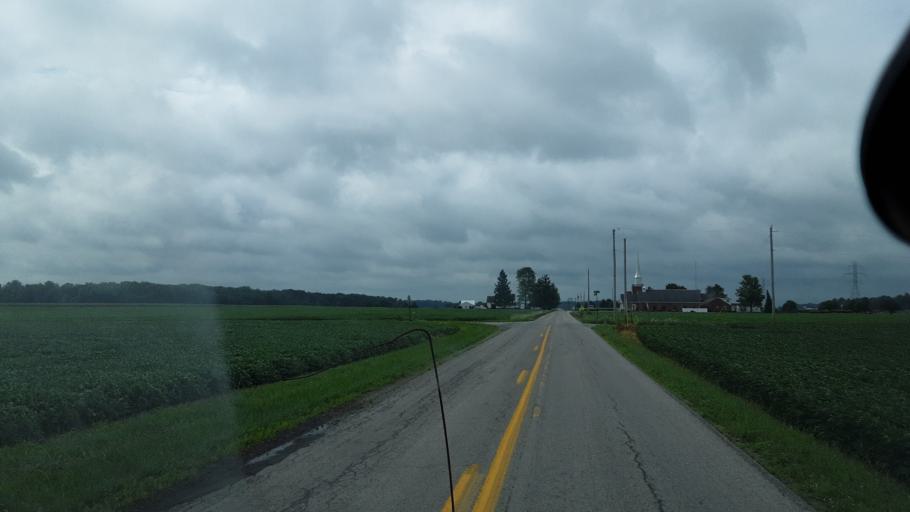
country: US
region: Indiana
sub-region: Allen County
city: Monroeville
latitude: 40.9713
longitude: -84.9691
